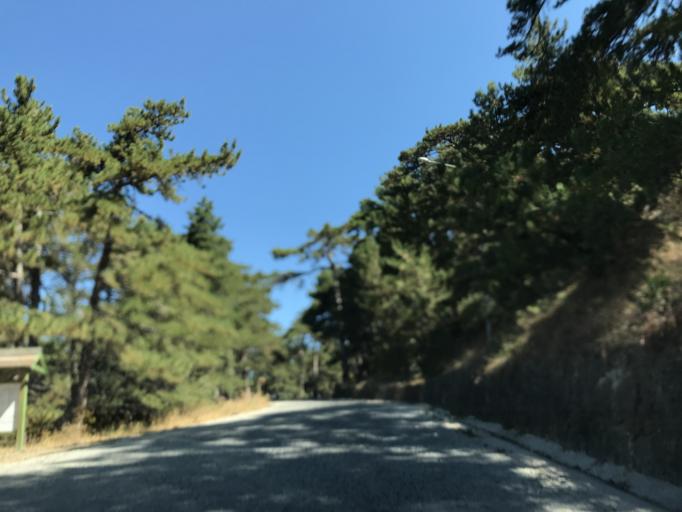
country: TR
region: Yozgat
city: Yozgat
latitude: 39.8048
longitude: 34.8102
